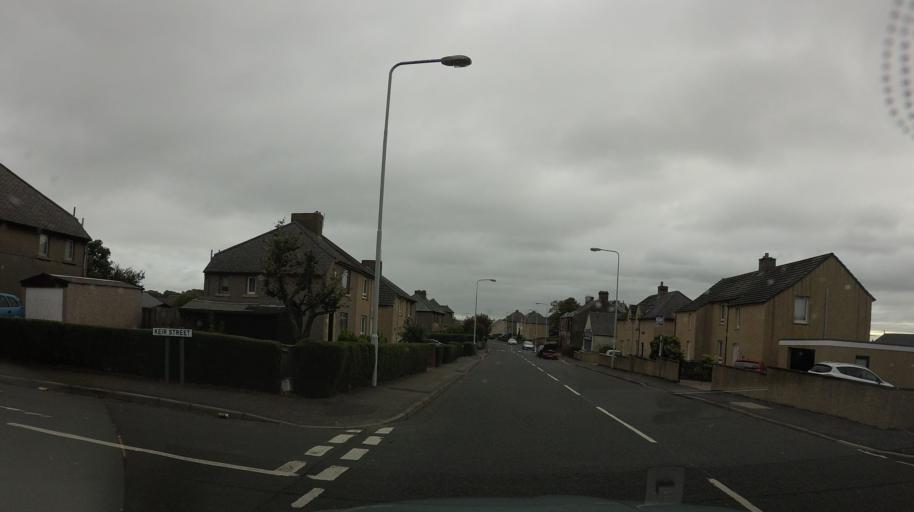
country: GB
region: Scotland
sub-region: Fife
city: Cowdenbeath
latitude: 56.1096
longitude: -3.3568
